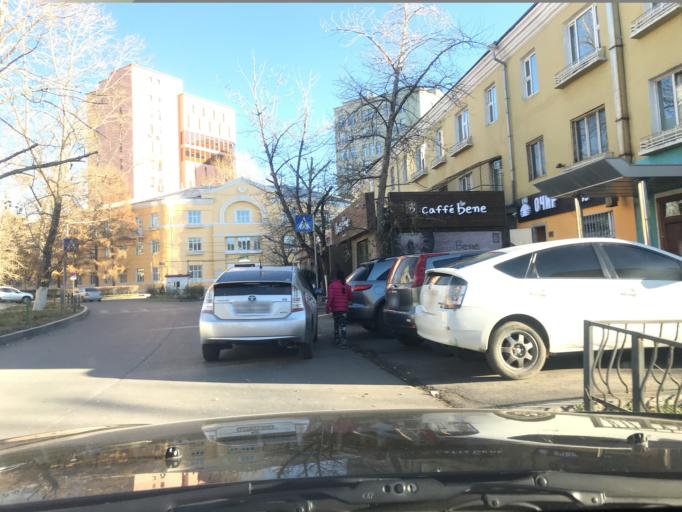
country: MN
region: Ulaanbaatar
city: Ulaanbaatar
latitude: 47.9244
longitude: 106.9128
